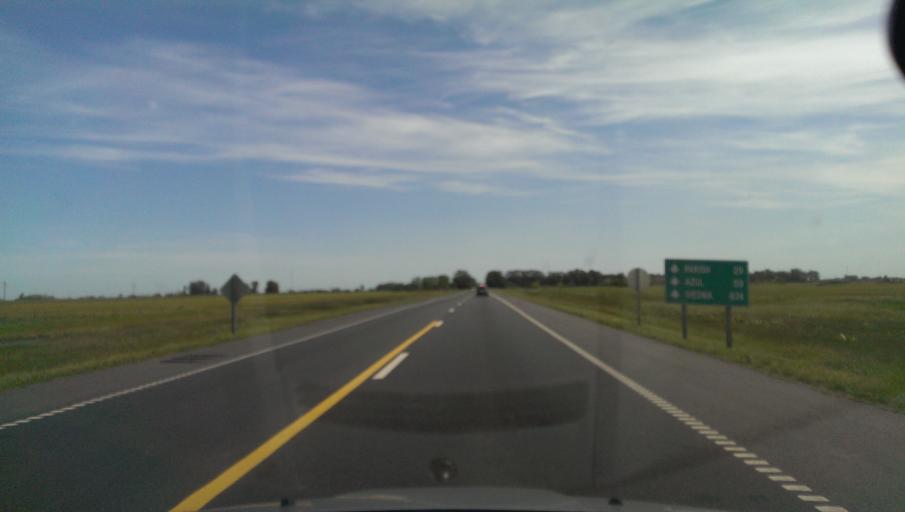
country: AR
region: Buenos Aires
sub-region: Partido de Las Flores
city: Las Flores
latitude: -36.3711
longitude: -59.4700
